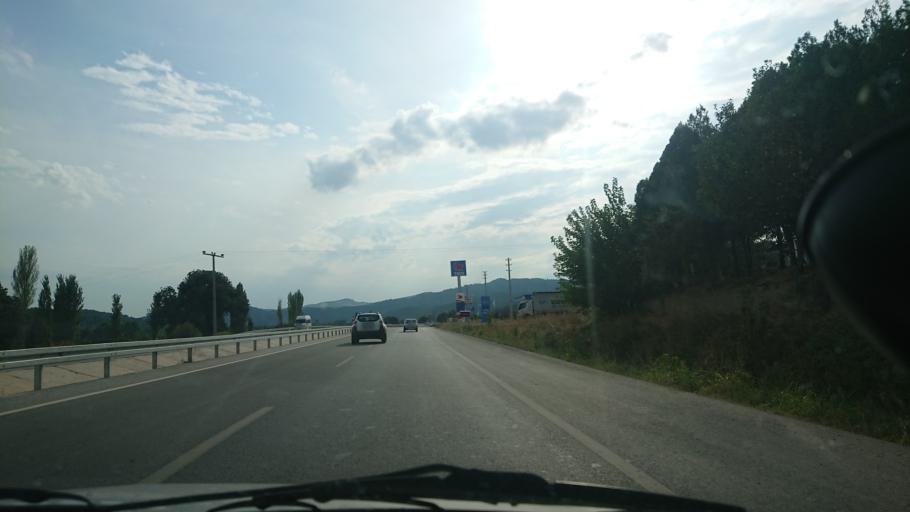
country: TR
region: Kuetahya
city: Gediz
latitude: 38.9374
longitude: 29.3164
